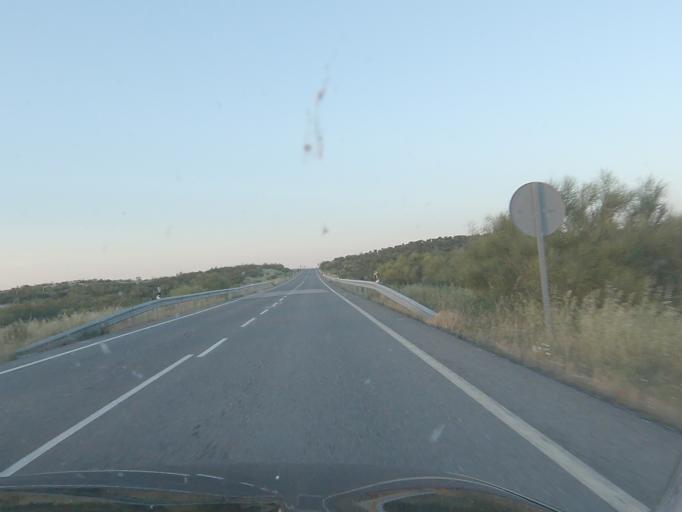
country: ES
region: Extremadura
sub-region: Provincia de Caceres
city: Salorino
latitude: 39.6028
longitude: -6.9766
